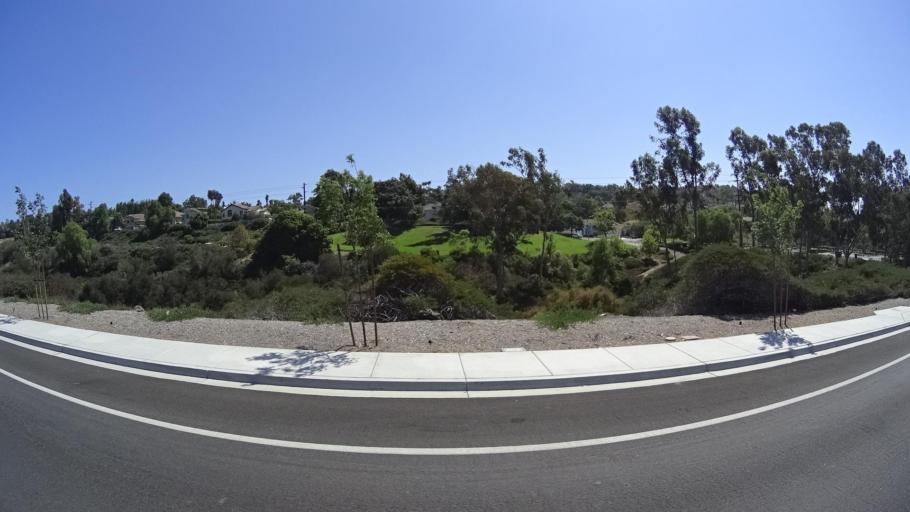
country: US
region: California
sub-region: San Diego County
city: Lake San Marcos
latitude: 33.1324
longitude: -117.2188
